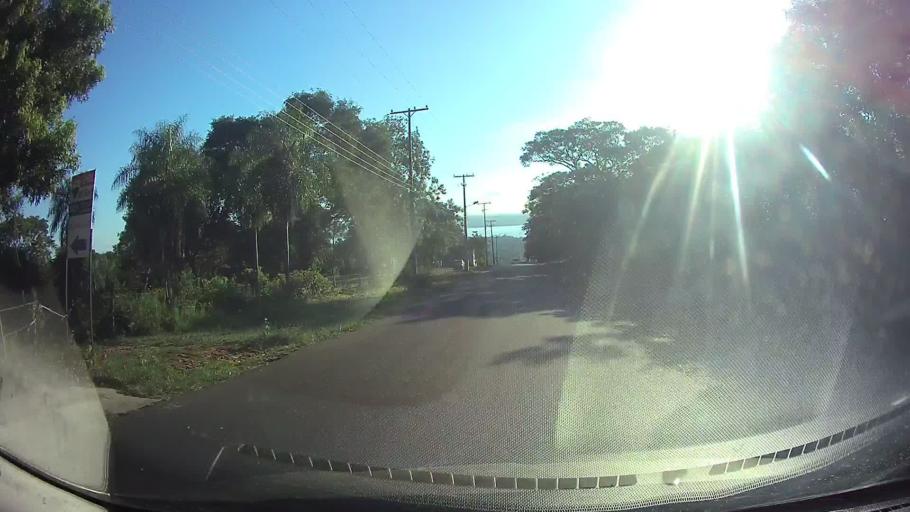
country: PY
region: Cordillera
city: San Bernardino
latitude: -25.3143
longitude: -57.2645
